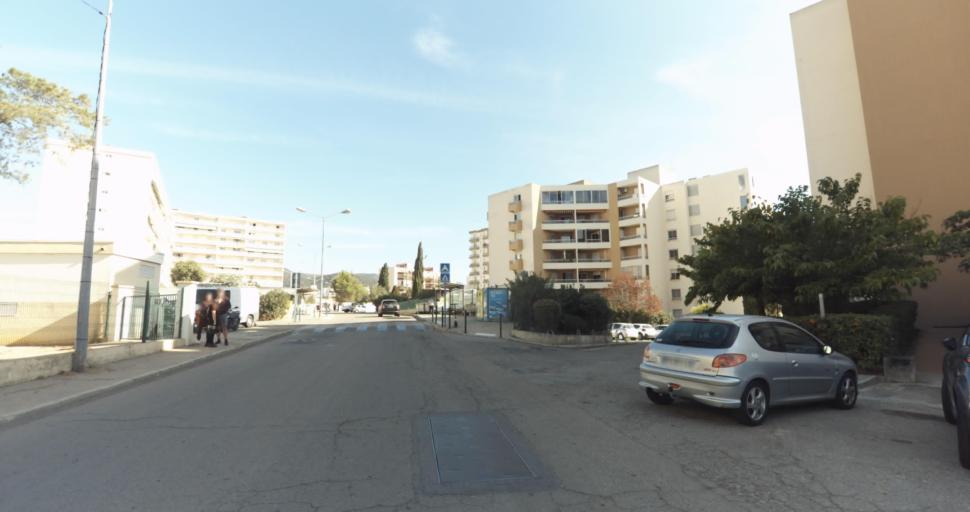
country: FR
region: Corsica
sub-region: Departement de la Corse-du-Sud
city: Ajaccio
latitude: 41.9388
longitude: 8.7455
